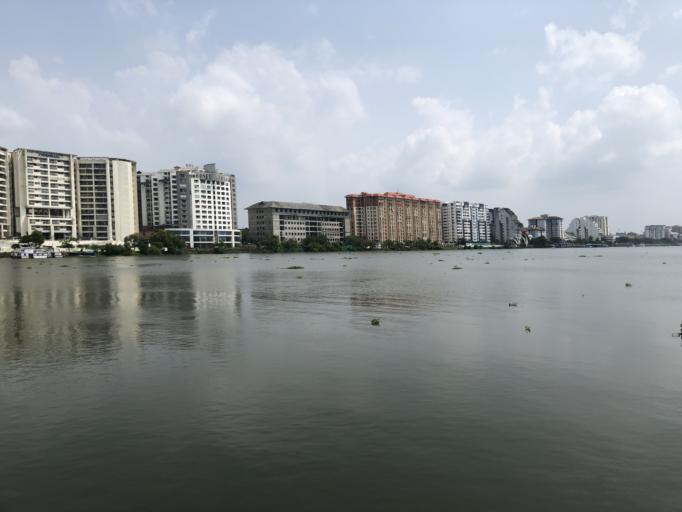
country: IN
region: Kerala
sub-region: Ernakulam
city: Cochin
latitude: 9.9899
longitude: 76.2674
